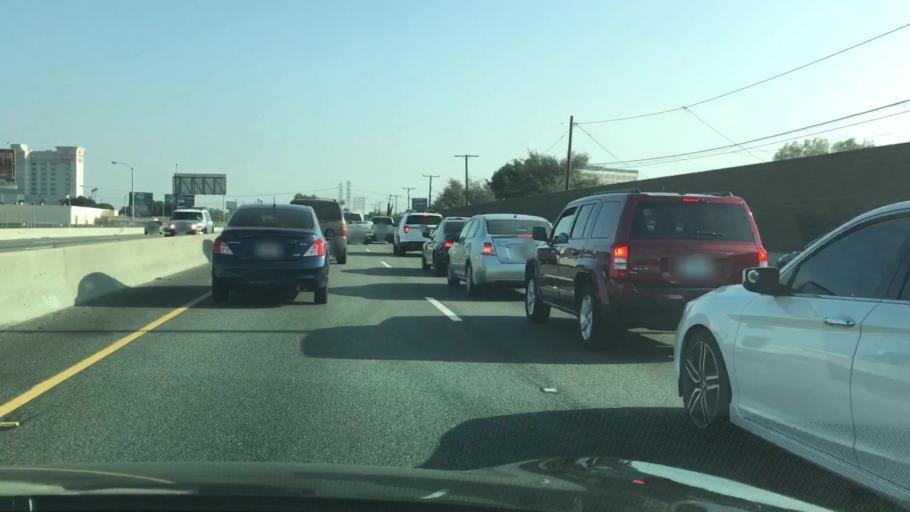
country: US
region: California
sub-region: Los Angeles County
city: Commerce
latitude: 34.0018
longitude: -118.1504
